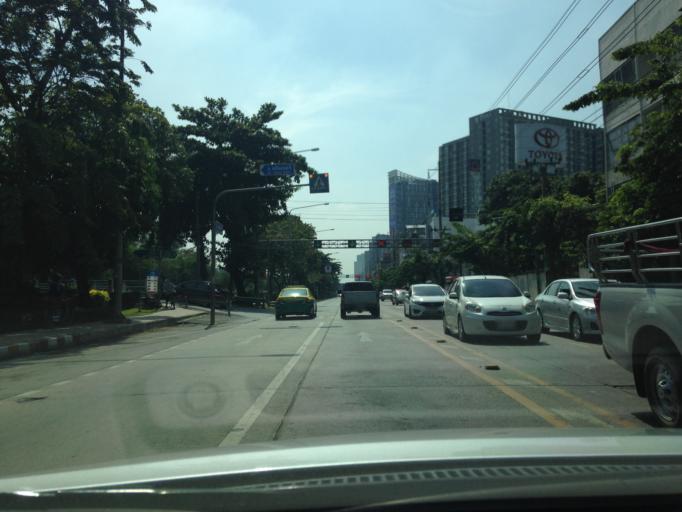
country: TH
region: Bangkok
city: Bang Sue
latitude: 13.8275
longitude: 100.5384
